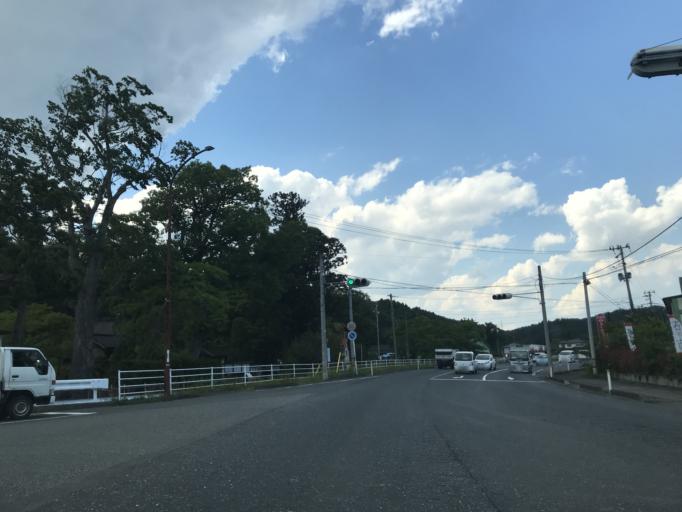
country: JP
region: Miyagi
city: Wakuya
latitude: 38.5460
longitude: 141.1412
